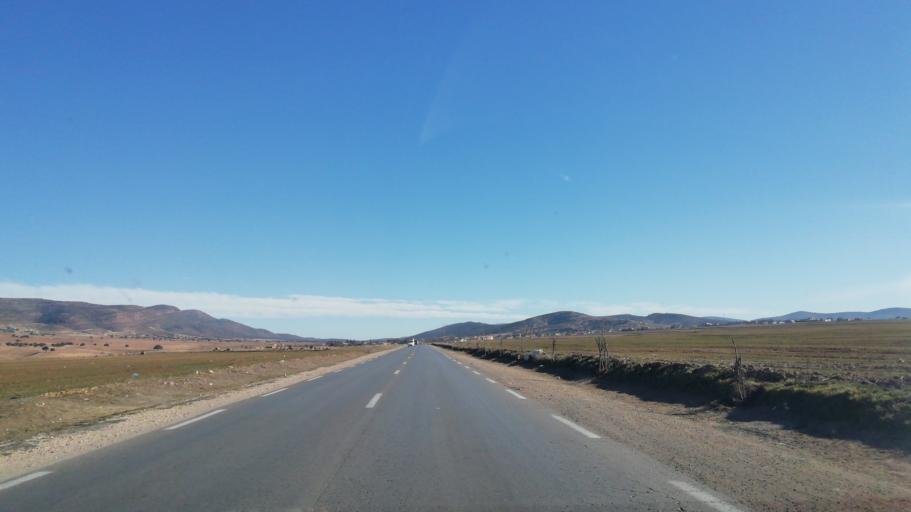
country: DZ
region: Tlemcen
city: Sebdou
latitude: 34.6666
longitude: -1.2852
